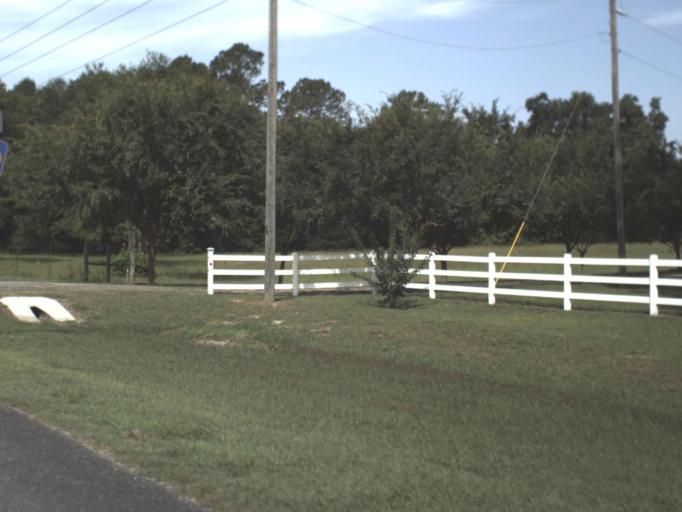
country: US
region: Florida
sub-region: Suwannee County
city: Live Oak
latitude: 30.2480
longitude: -83.0451
